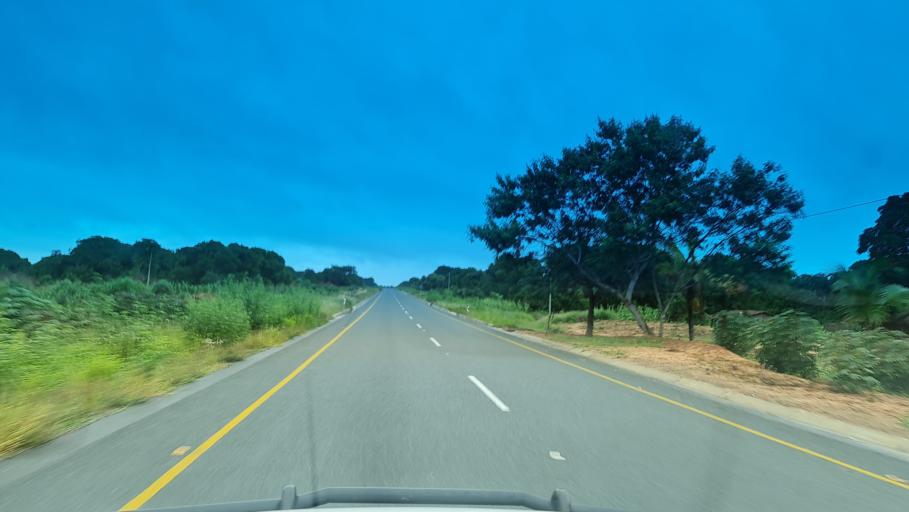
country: MZ
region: Nampula
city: Nampula
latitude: -15.6190
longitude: 39.3336
